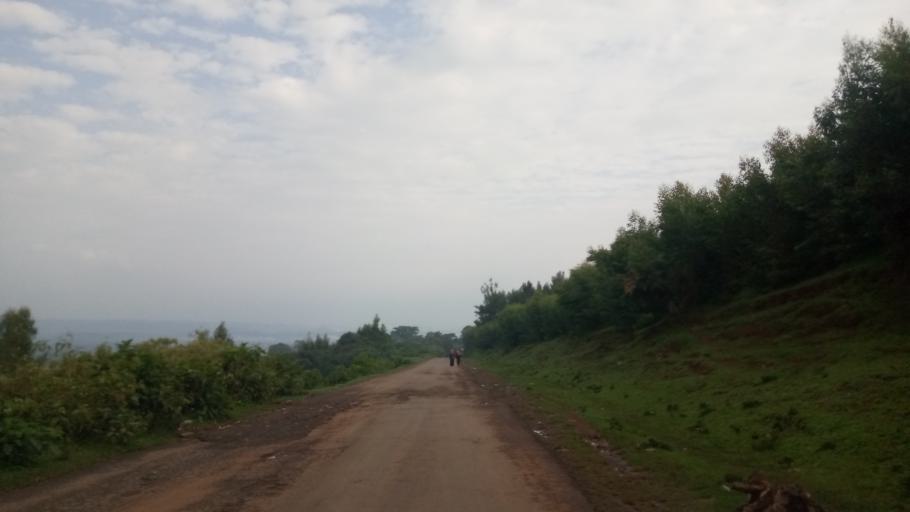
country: ET
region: Oromiya
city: Agaro
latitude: 7.7937
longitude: 36.7240
